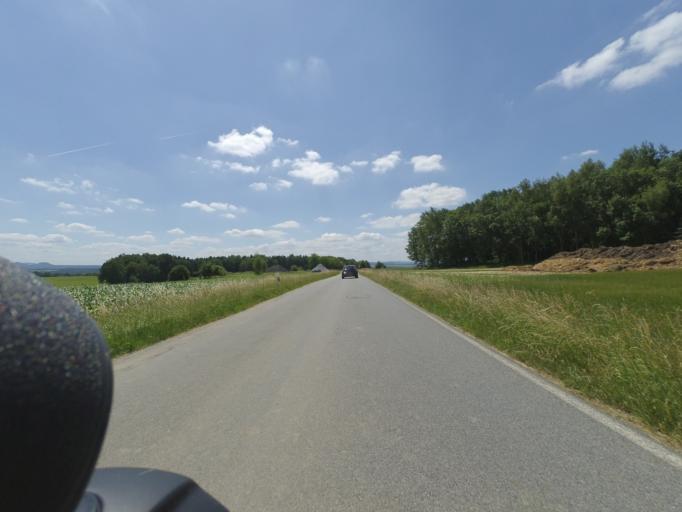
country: DE
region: Saxony
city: Stadt Wehlen
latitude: 50.9748
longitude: 14.0201
